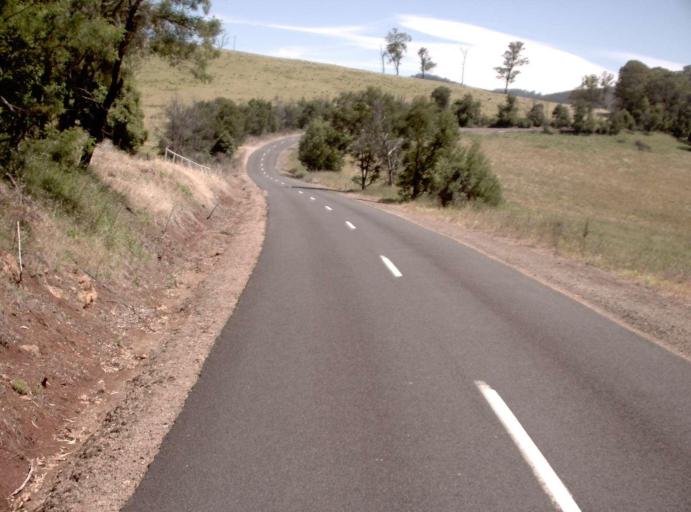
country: AU
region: Victoria
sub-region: East Gippsland
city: Lakes Entrance
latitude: -37.4062
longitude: 148.2115
